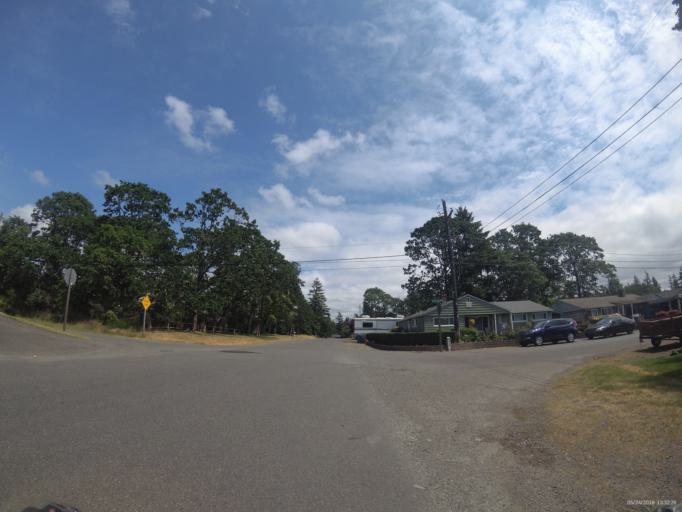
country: US
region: Washington
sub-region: Pierce County
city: Lakewood
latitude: 47.1796
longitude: -122.5301
